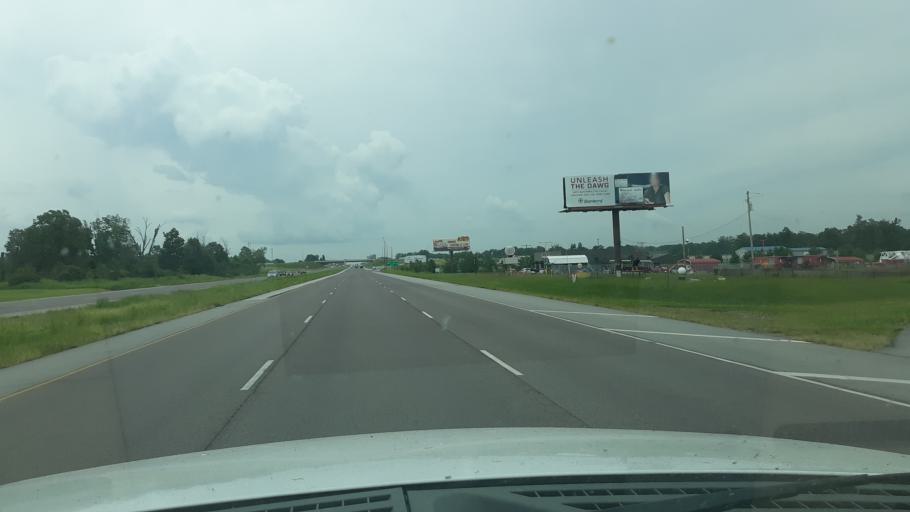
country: US
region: Illinois
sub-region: Williamson County
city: Crainville
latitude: 37.7450
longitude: -89.0682
